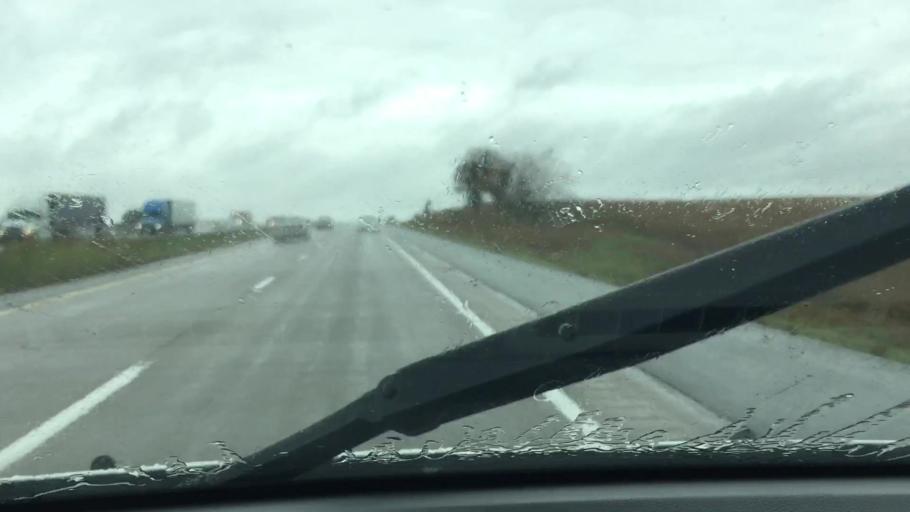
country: US
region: Iowa
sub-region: Poweshiek County
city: Brooklyn
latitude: 41.6953
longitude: -92.5145
